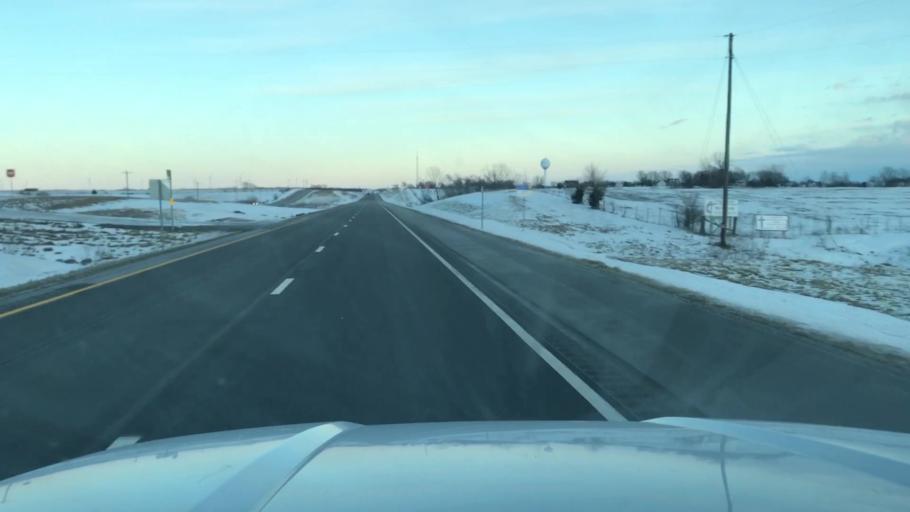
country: US
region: Missouri
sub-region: Clinton County
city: Gower
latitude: 39.7619
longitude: -94.5178
